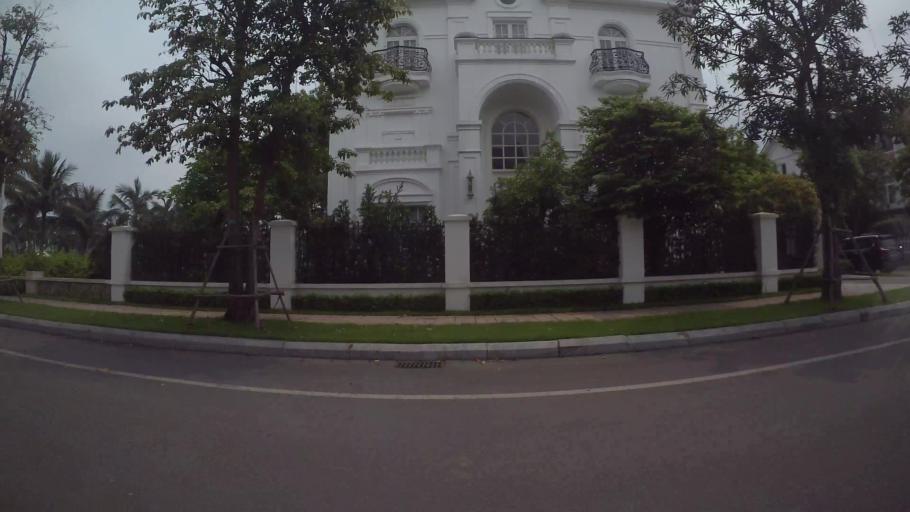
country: VN
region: Ha Noi
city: Trau Quy
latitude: 21.0433
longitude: 105.9155
